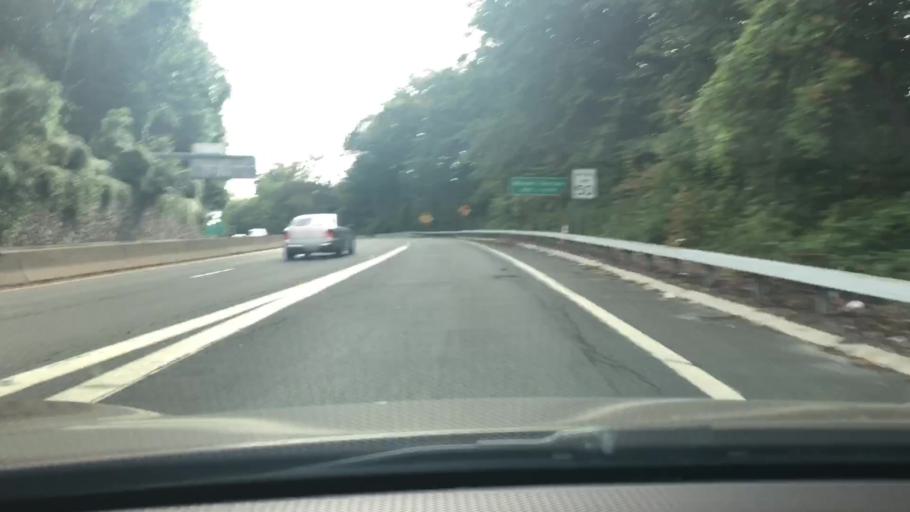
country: US
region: New York
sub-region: Westchester County
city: Pelham
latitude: 40.9248
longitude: -73.8080
